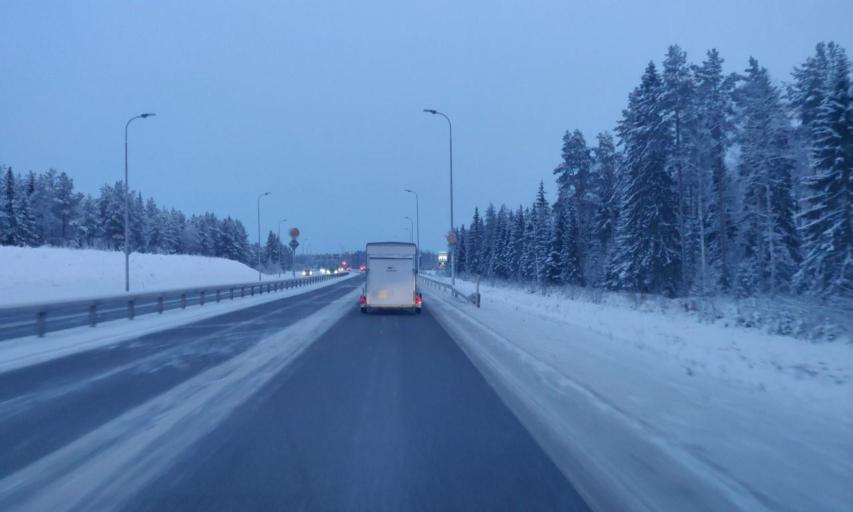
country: FI
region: Northern Ostrobothnia
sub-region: Oulu
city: Kempele
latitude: 64.9823
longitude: 25.5553
